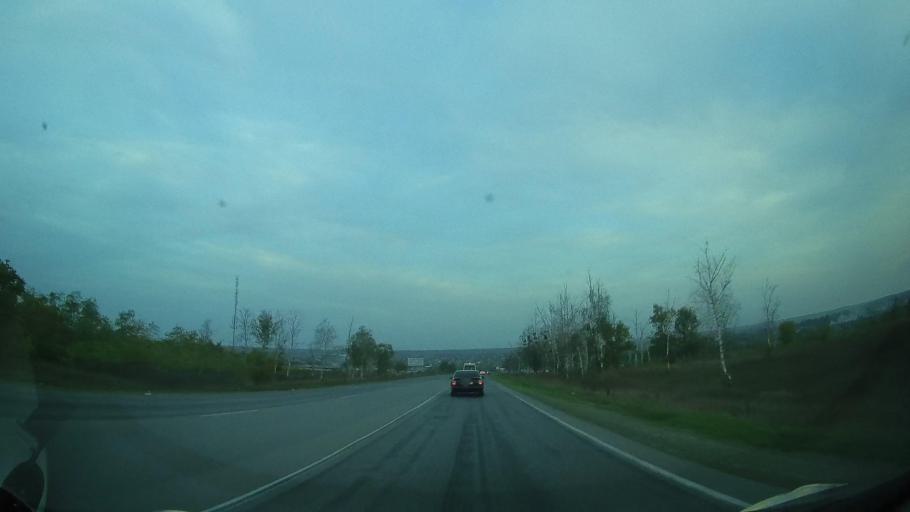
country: RU
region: Rostov
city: Kagal'nitskaya
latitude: 46.8891
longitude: 40.1372
